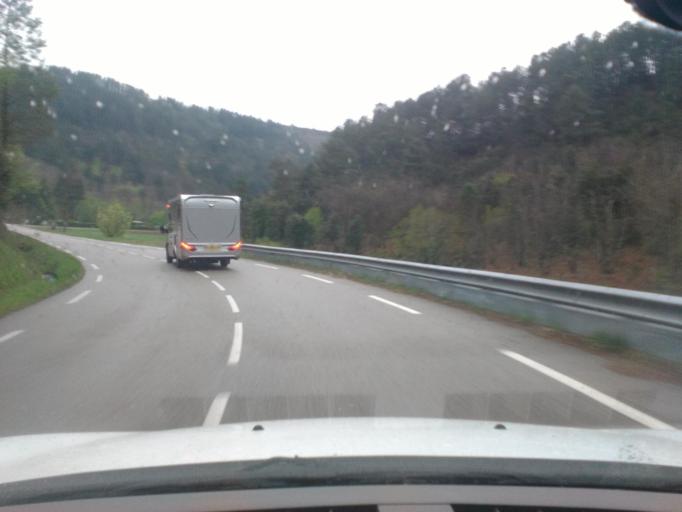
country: FR
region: Languedoc-Roussillon
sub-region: Departement du Gard
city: Lasalle
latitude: 44.1164
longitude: 3.7732
